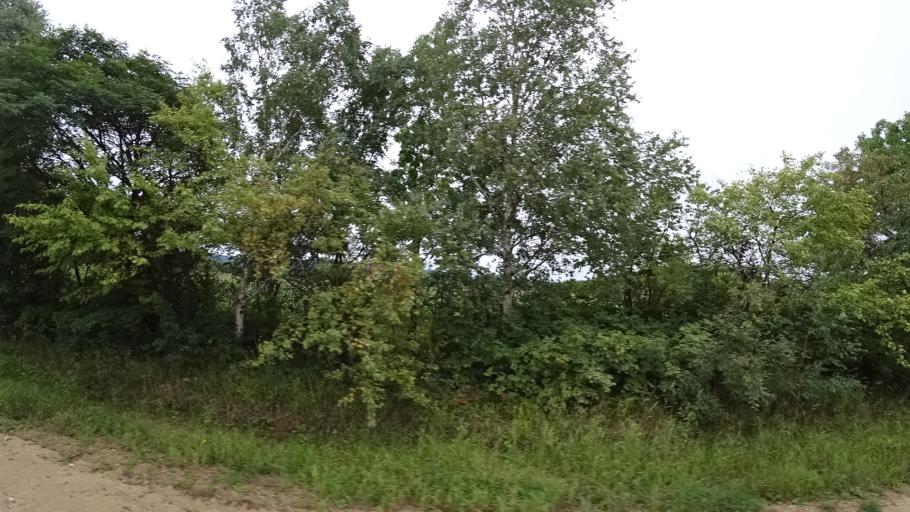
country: RU
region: Primorskiy
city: Rettikhovka
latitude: 44.1598
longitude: 132.6899
